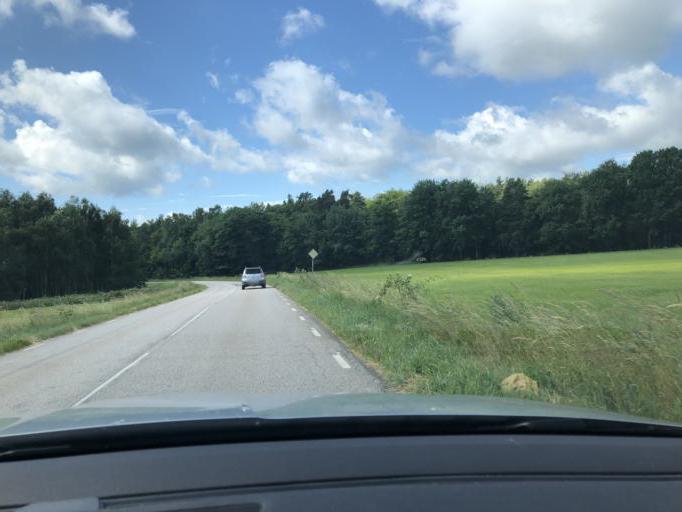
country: SE
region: Blekinge
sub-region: Solvesborgs Kommun
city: Soelvesborg
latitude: 56.1169
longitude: 14.6223
